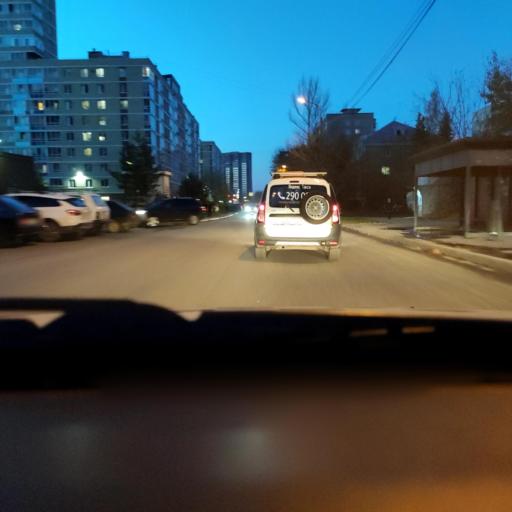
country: RU
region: Perm
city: Kondratovo
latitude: 57.9934
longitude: 56.1484
